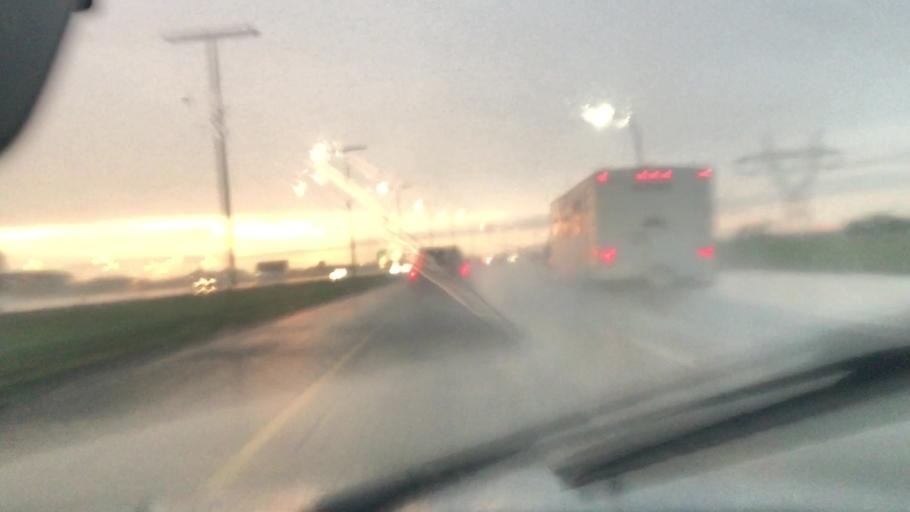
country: CA
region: Alberta
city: Devon
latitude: 53.4328
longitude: -113.5877
